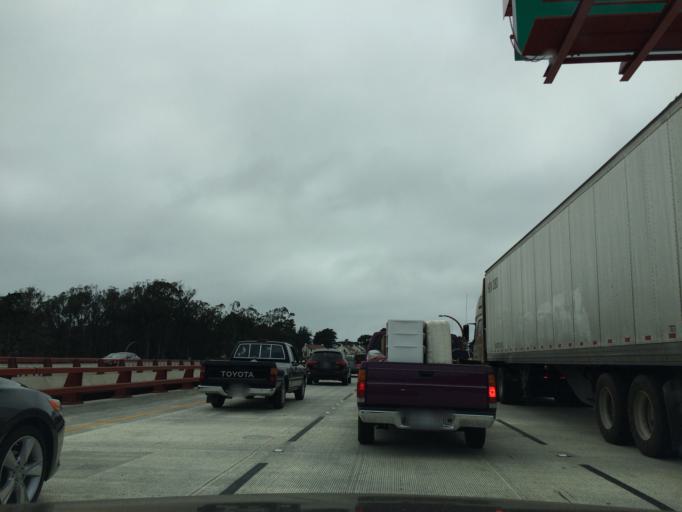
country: US
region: California
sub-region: San Francisco County
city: San Francisco
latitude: 37.8025
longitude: -122.4666
